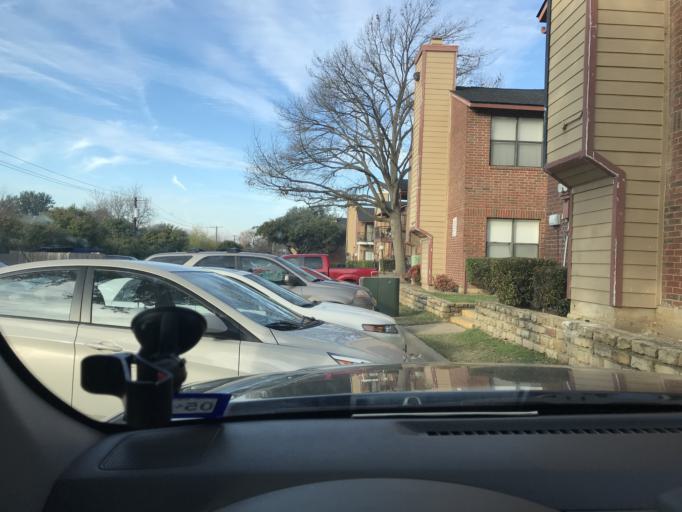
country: US
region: Texas
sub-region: Dallas County
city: Richardson
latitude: 32.9078
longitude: -96.7422
